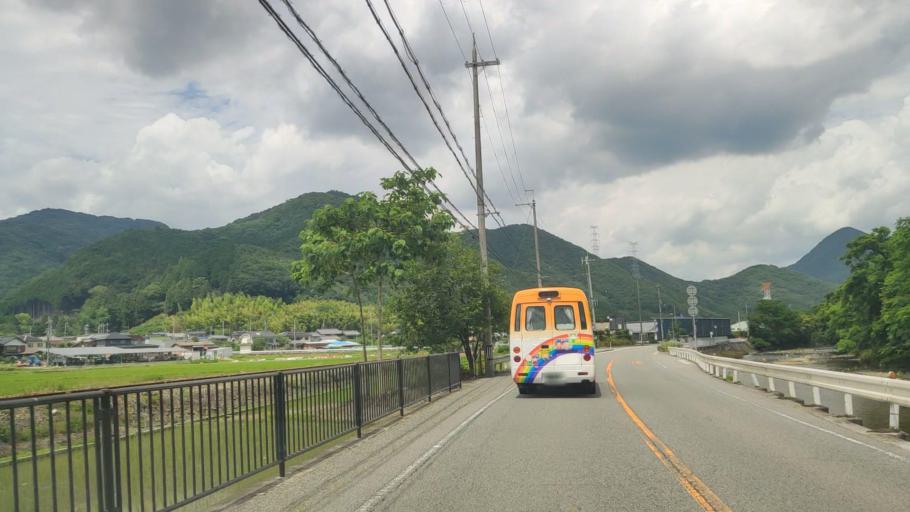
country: JP
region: Hyogo
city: Yamazakicho-nakabirose
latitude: 34.9404
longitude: 134.4875
